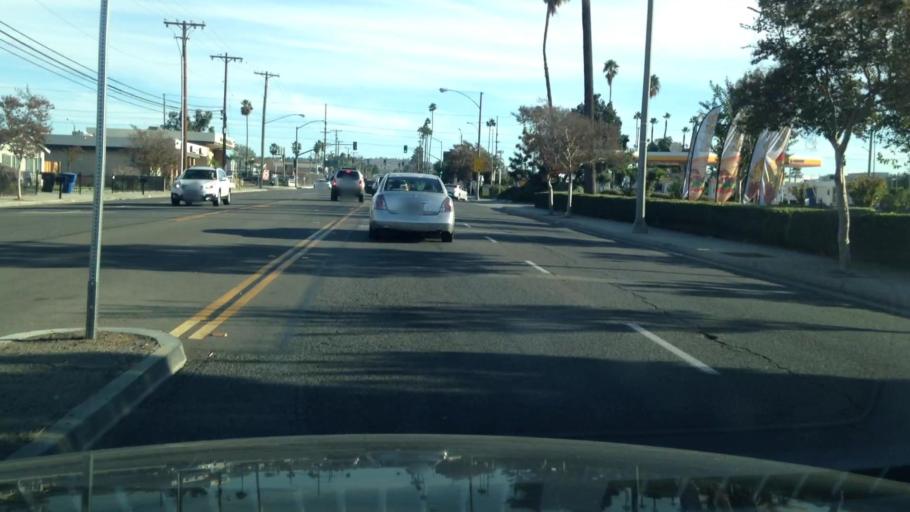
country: US
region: California
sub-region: Riverside County
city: Riverside
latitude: 33.9290
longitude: -117.4210
